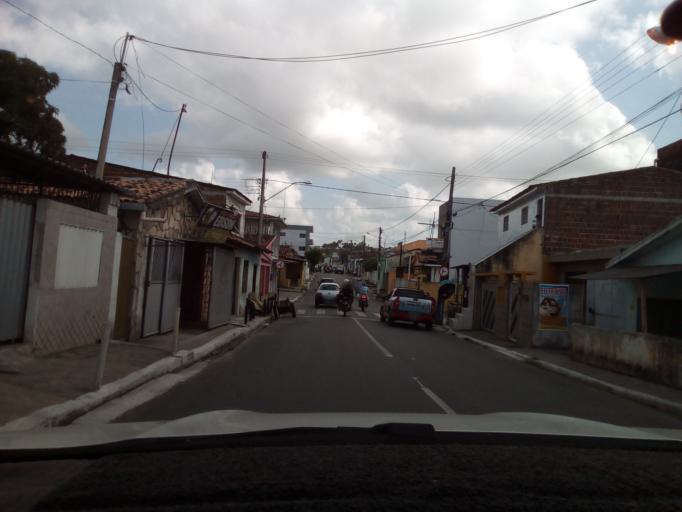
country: BR
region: Paraiba
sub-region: Bayeux
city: Bayeux
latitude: -7.1279
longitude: -34.9315
